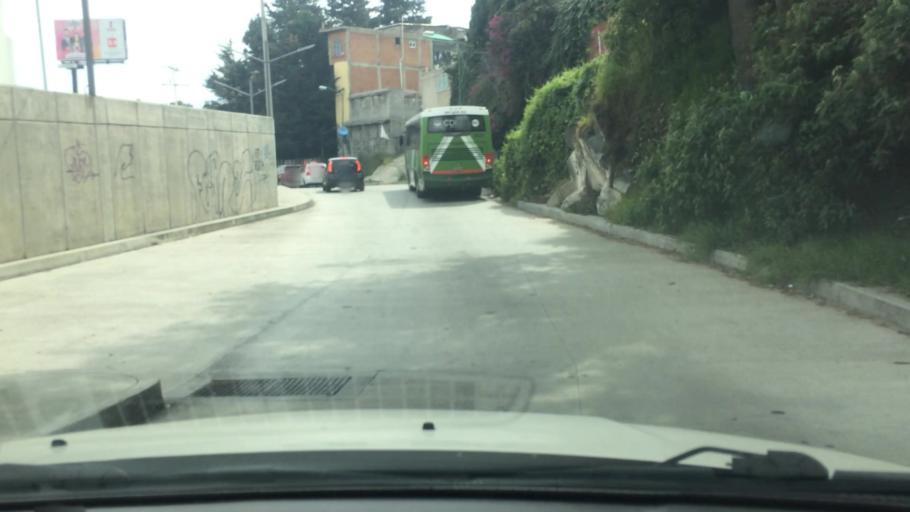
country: MX
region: Mexico City
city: Xochimilco
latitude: 19.2409
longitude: -99.1485
